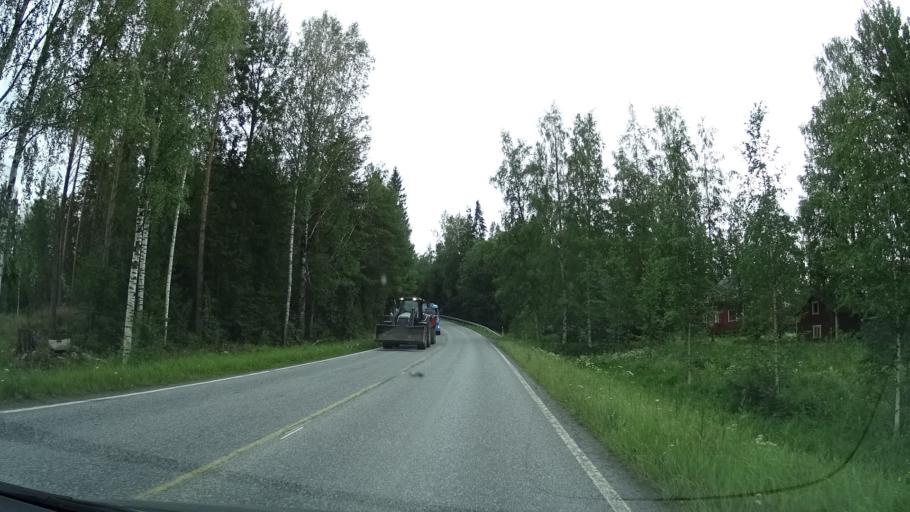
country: FI
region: Pirkanmaa
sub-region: Etelae-Pirkanmaa
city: Urjala
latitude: 61.0885
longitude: 23.5139
